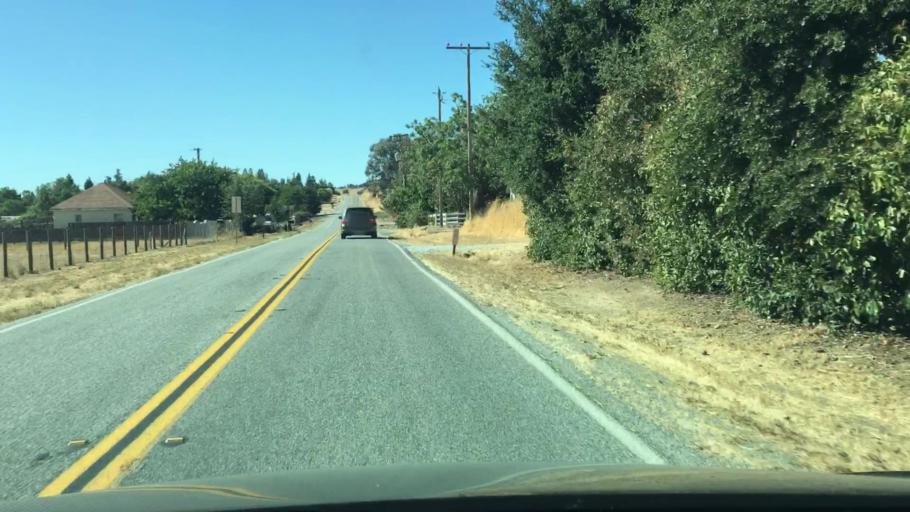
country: US
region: California
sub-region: Santa Clara County
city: San Martin
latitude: 37.0885
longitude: -121.5676
